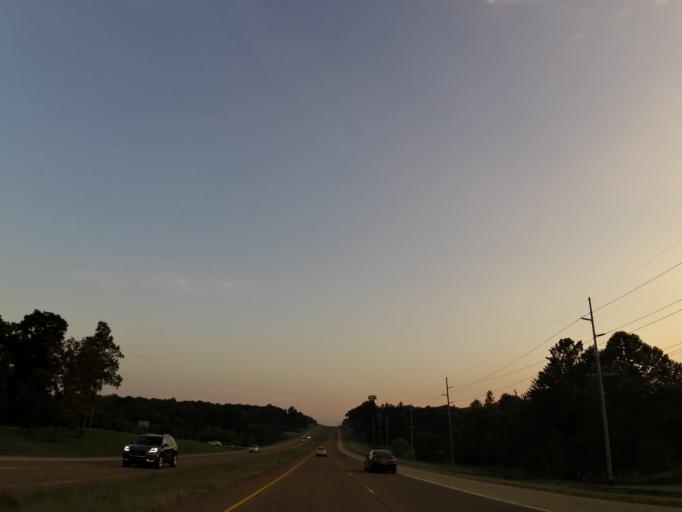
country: US
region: Tennessee
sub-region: Henry County
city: Paris
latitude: 36.2646
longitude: -88.3390
